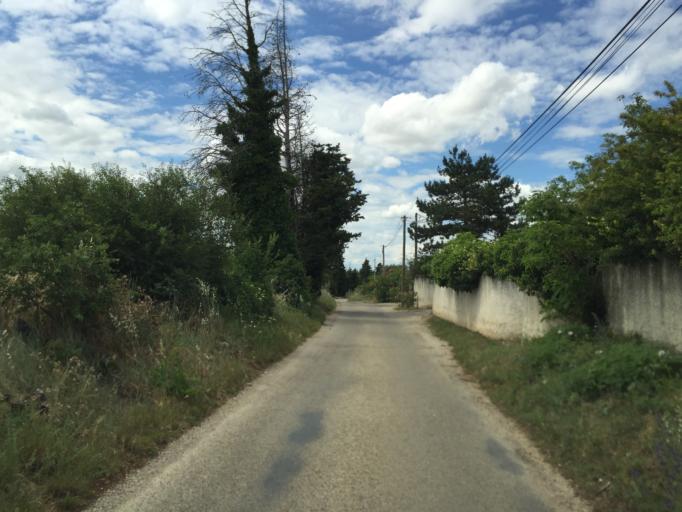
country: FR
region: Provence-Alpes-Cote d'Azur
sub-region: Departement du Vaucluse
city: Sorgues
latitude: 44.0223
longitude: 4.8566
